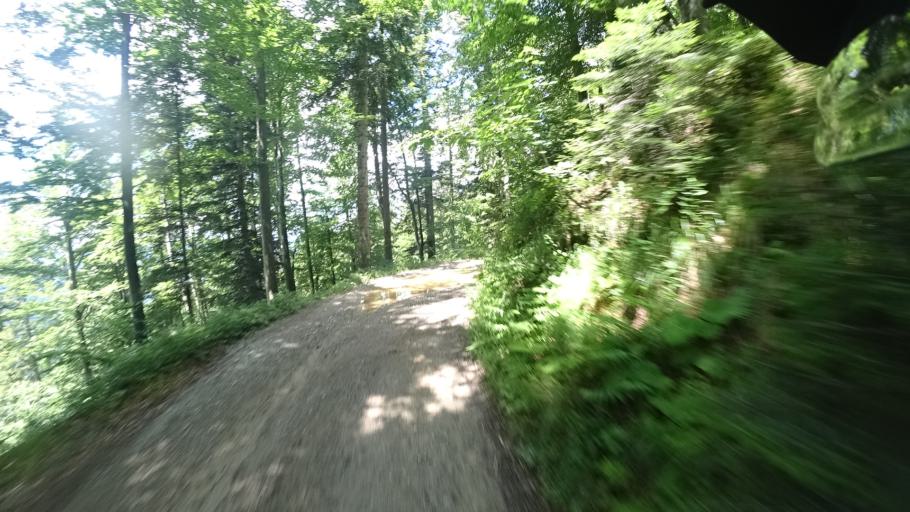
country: SI
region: Osilnica
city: Osilnica
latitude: 45.4721
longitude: 14.7363
